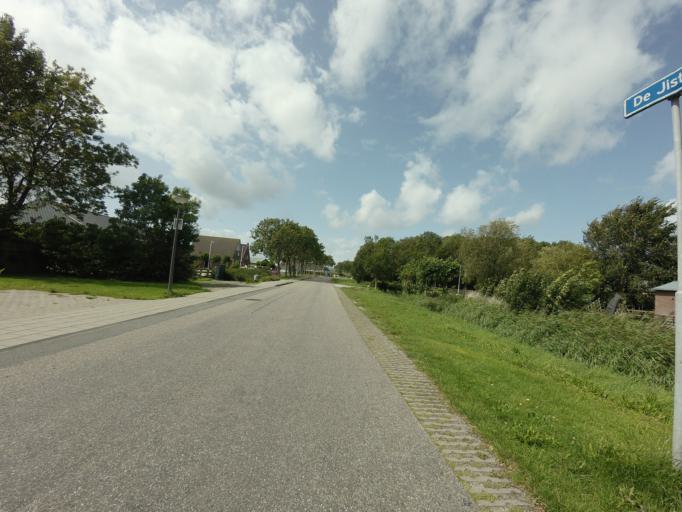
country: NL
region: Friesland
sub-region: Gemeente Harlingen
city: Harlingen
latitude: 53.1483
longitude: 5.4803
